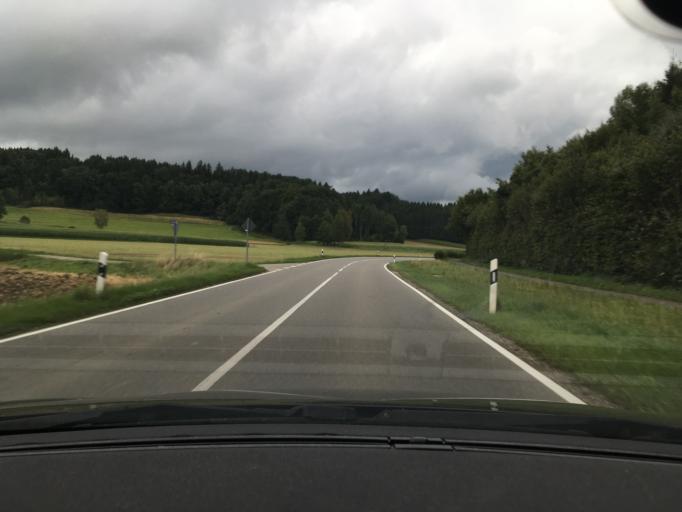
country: DE
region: Baden-Wuerttemberg
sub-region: Tuebingen Region
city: Markdorf
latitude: 47.7729
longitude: 9.4128
